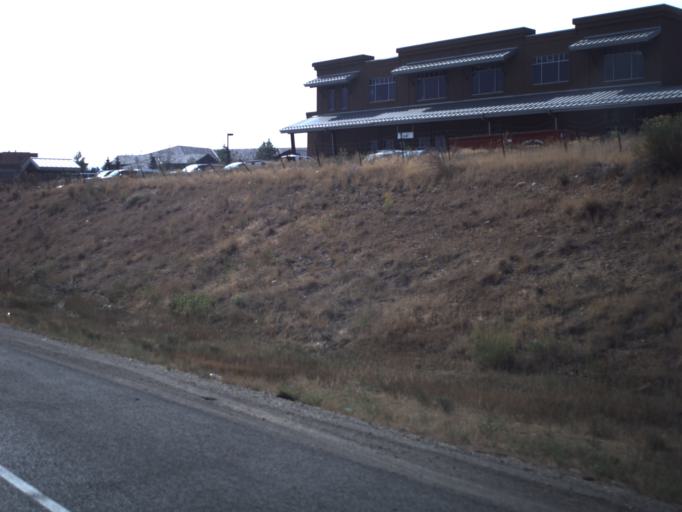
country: US
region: Utah
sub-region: Summit County
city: Snyderville
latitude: 40.7259
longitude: -111.5416
